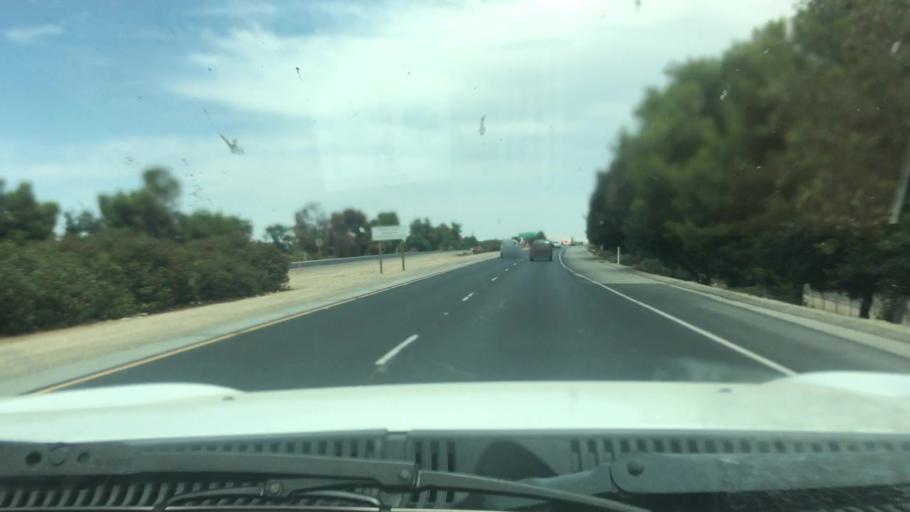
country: US
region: California
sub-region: Tulare County
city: Porterville
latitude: 36.0702
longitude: -119.0394
